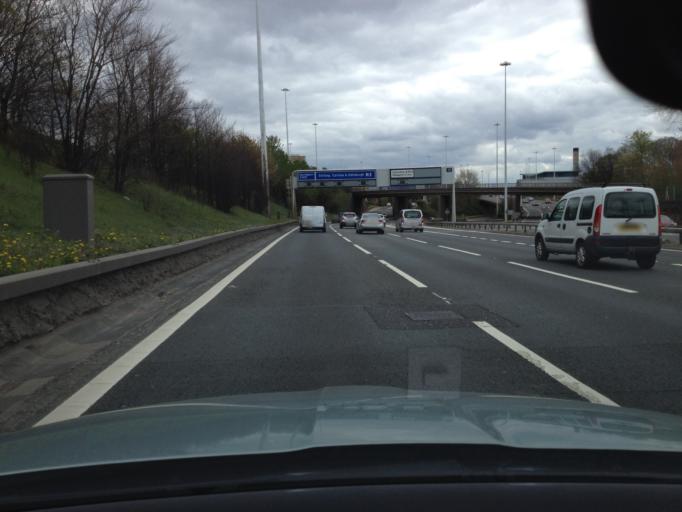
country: GB
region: Scotland
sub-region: Glasgow City
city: Glasgow
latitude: 55.8694
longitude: -4.2415
